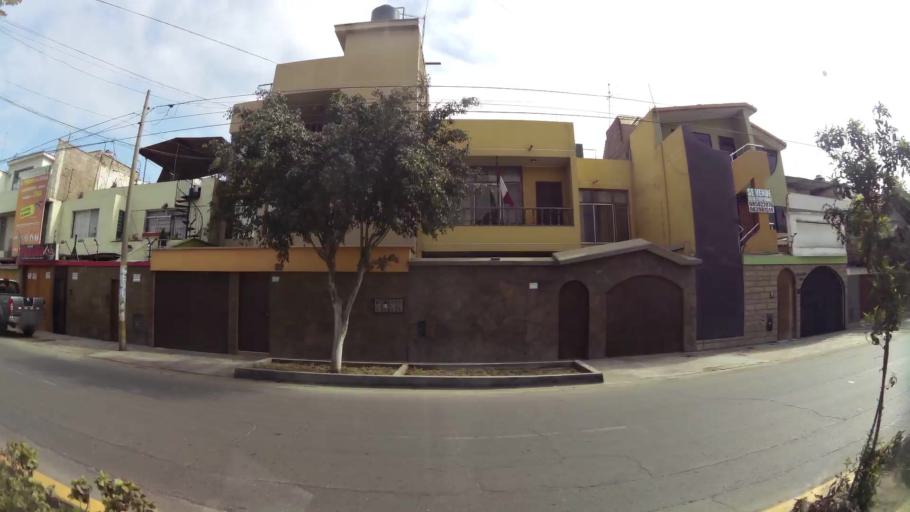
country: PE
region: Ica
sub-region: Provincia de Ica
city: Ica
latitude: -14.0729
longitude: -75.7302
